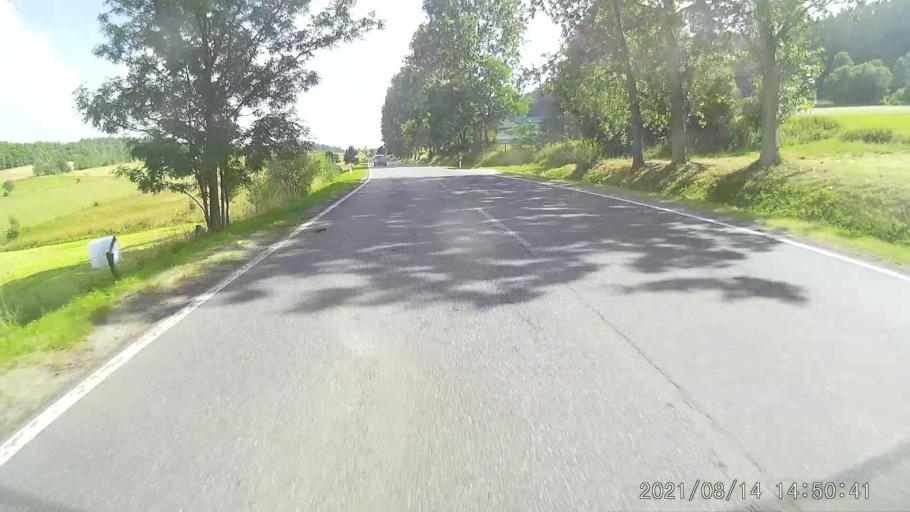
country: PL
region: Lower Silesian Voivodeship
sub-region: Powiat walbrzyski
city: Gluszyca Gorna
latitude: 50.6546
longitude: 16.3762
